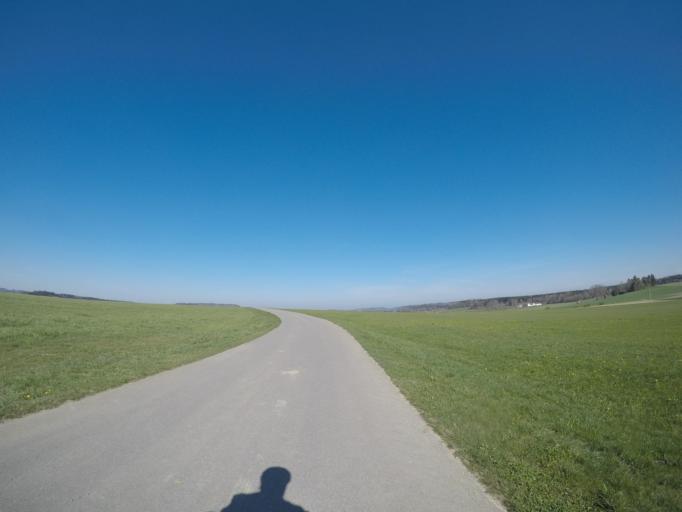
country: DE
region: Baden-Wuerttemberg
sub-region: Tuebingen Region
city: Fleischwangen
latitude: 47.8743
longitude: 9.4988
